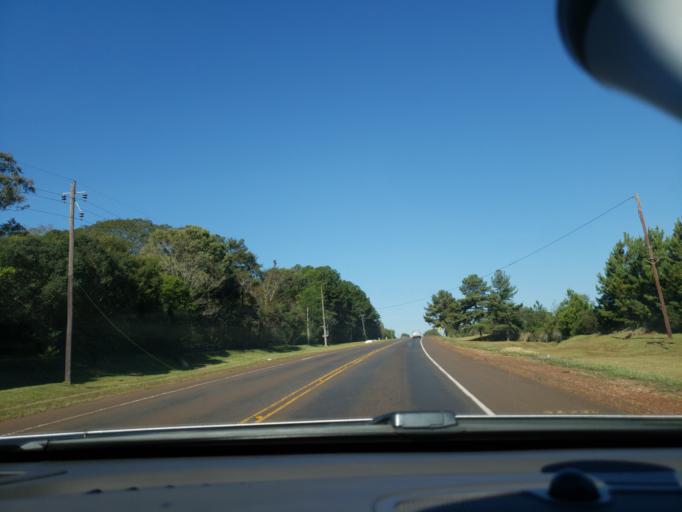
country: AR
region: Misiones
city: Garupa
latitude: -27.6083
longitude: -55.8222
